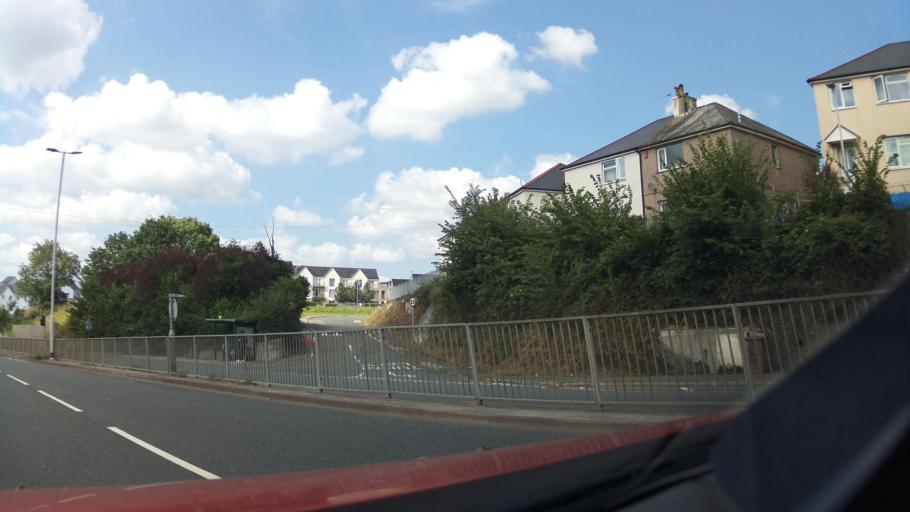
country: GB
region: England
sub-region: Cornwall
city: Millbrook
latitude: 50.3909
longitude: -4.1700
